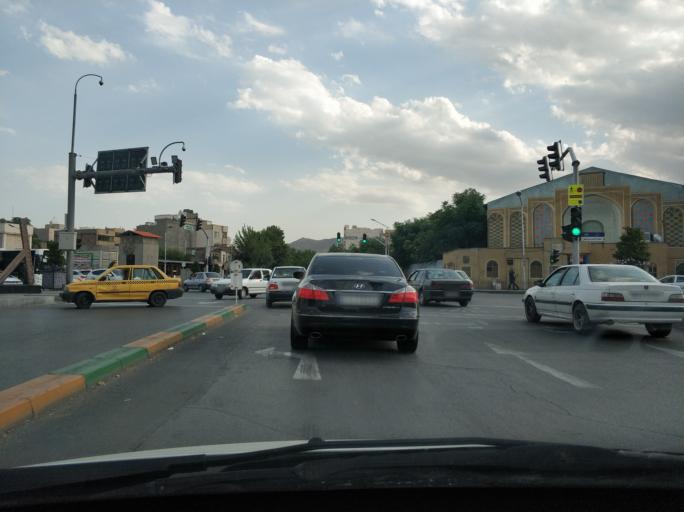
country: IR
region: Razavi Khorasan
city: Mashhad
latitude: 36.2816
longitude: 59.5960
